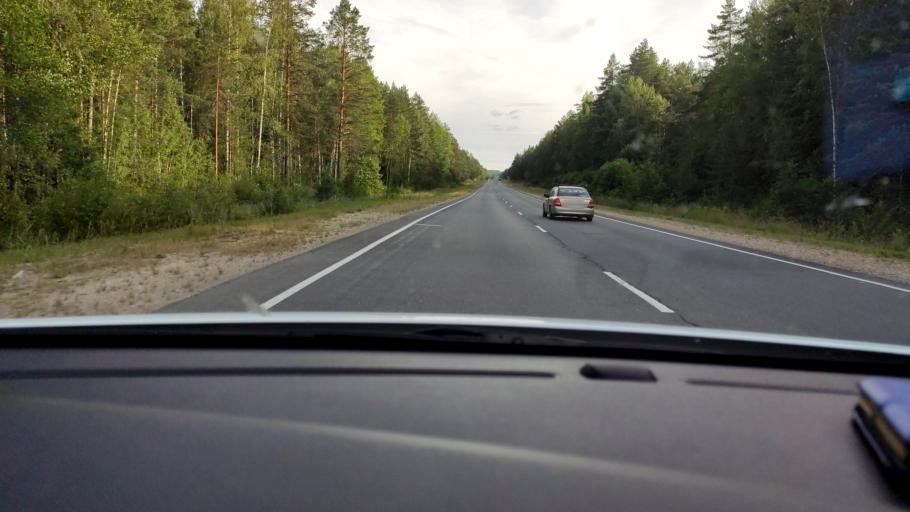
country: RU
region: Mariy-El
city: Suslonger
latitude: 56.3316
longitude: 48.2353
